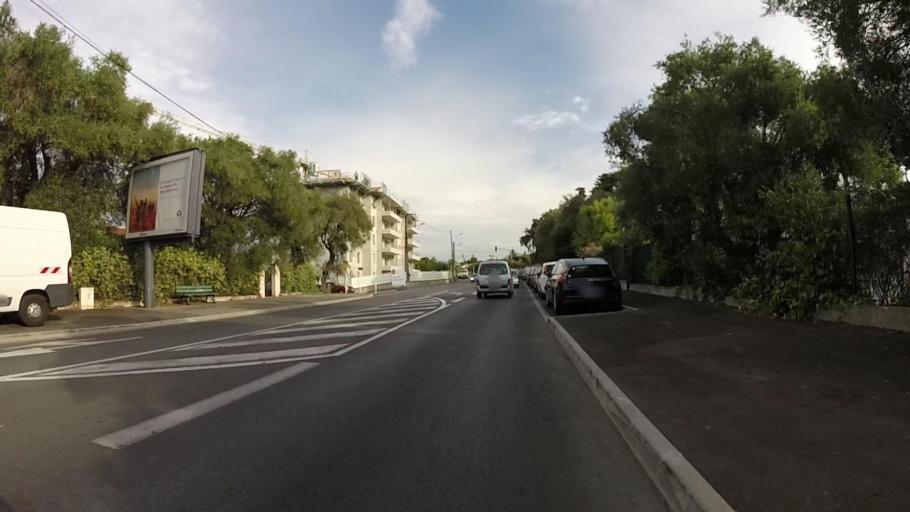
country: FR
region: Provence-Alpes-Cote d'Azur
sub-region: Departement des Alpes-Maritimes
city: Biot
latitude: 43.5954
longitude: 7.1065
